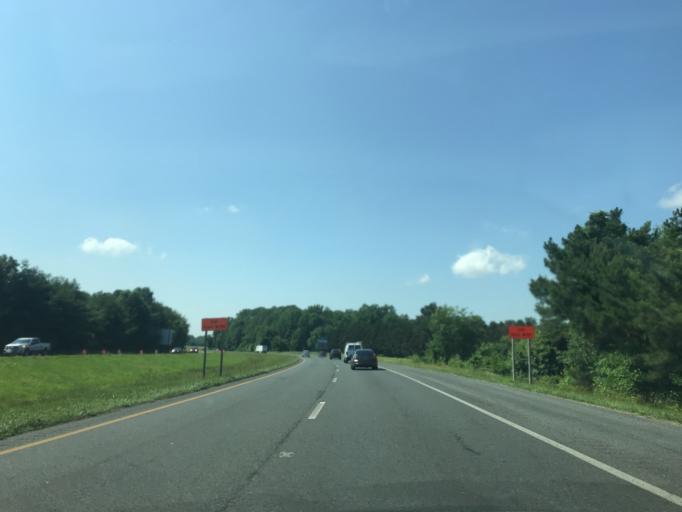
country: US
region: Maryland
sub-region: Wicomico County
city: Salisbury
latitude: 38.3870
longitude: -75.5415
